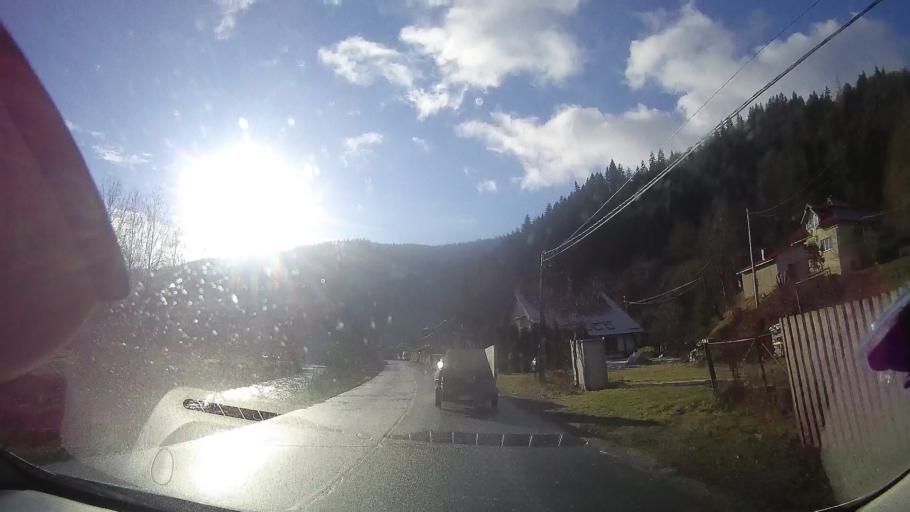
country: RO
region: Alba
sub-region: Comuna Vadu Motilor
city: Vadu Motilor
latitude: 46.3987
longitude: 22.9624
